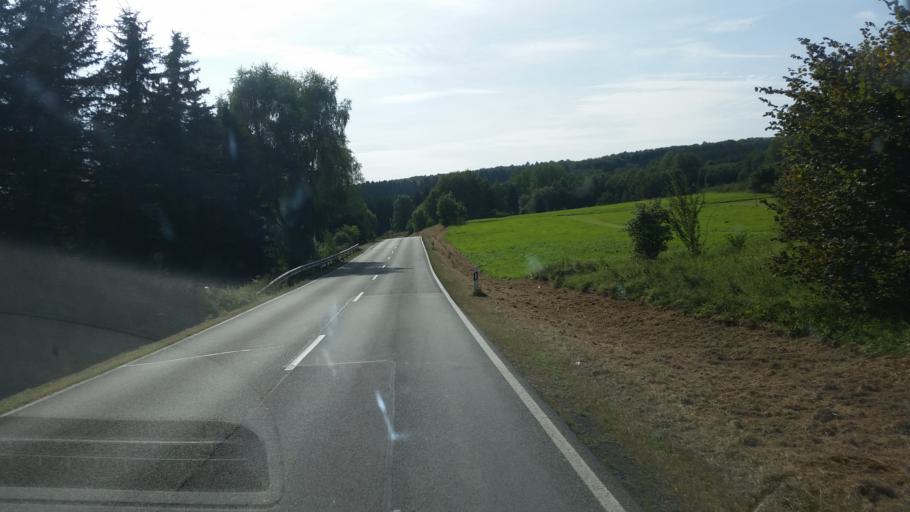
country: DE
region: Rheinland-Pfalz
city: Brandscheid
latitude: 50.5728
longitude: 7.9100
